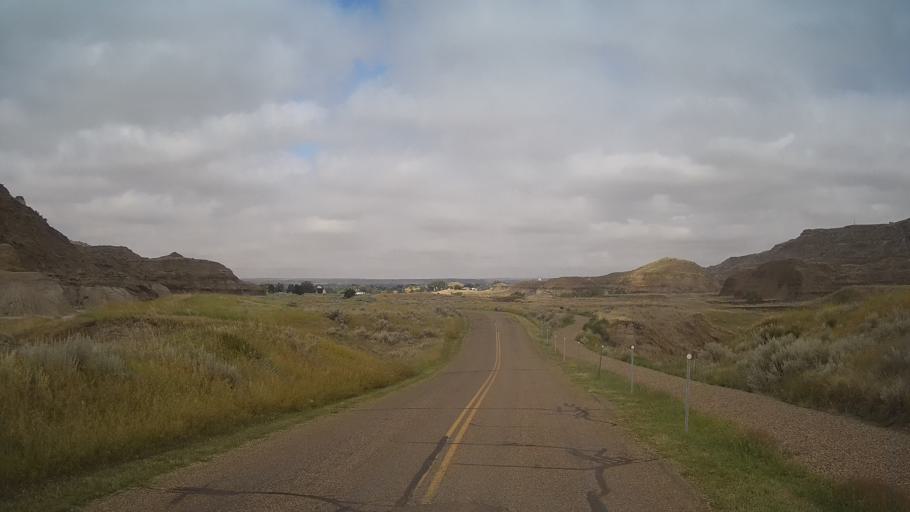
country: US
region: Montana
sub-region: Dawson County
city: Glendive
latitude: 47.0849
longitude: -104.6990
